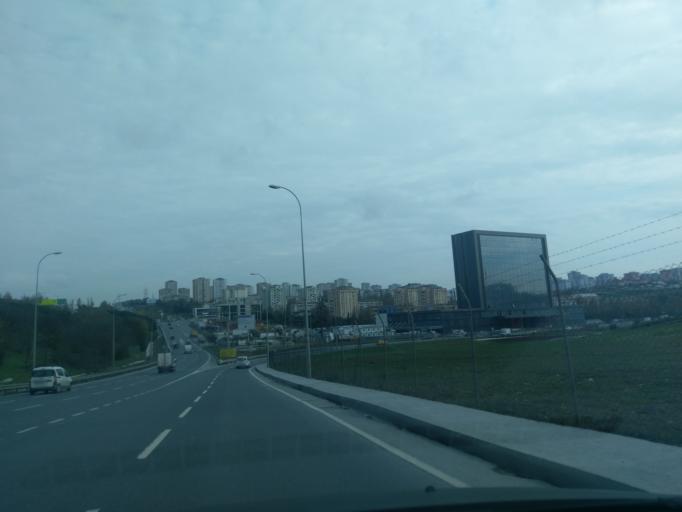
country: TR
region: Istanbul
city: Basaksehir
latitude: 41.0616
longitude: 28.7709
